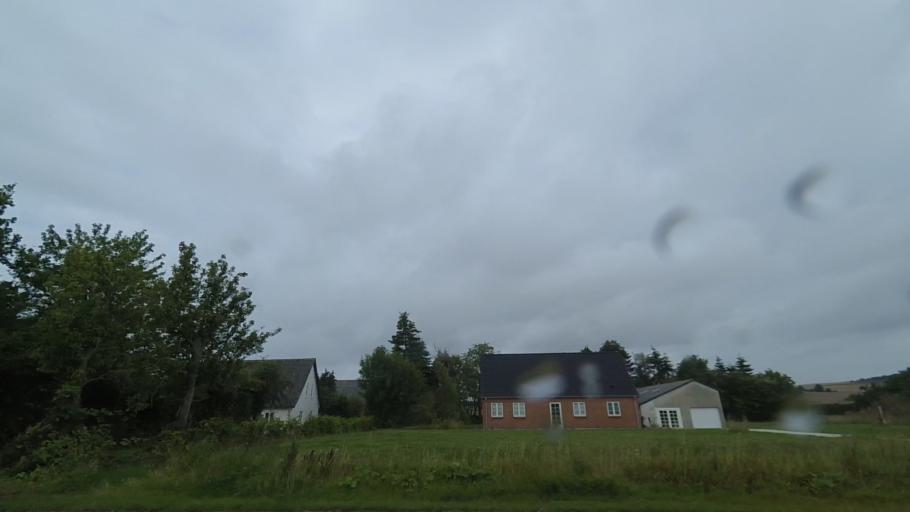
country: DK
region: Central Jutland
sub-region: Syddjurs Kommune
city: Ronde
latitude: 56.3128
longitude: 10.4616
